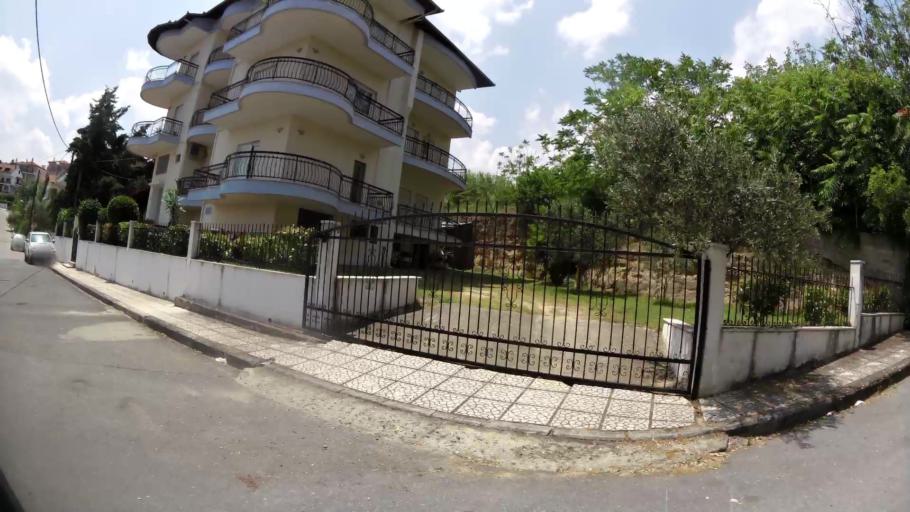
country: GR
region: Central Macedonia
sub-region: Nomos Imathias
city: Veroia
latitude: 40.5154
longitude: 22.1873
